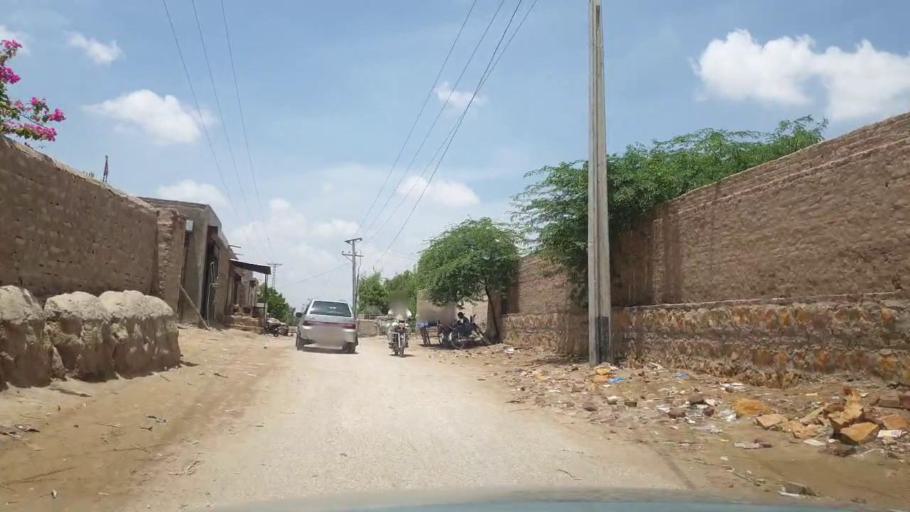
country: PK
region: Sindh
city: Kot Diji
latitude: 27.1602
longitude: 68.9652
